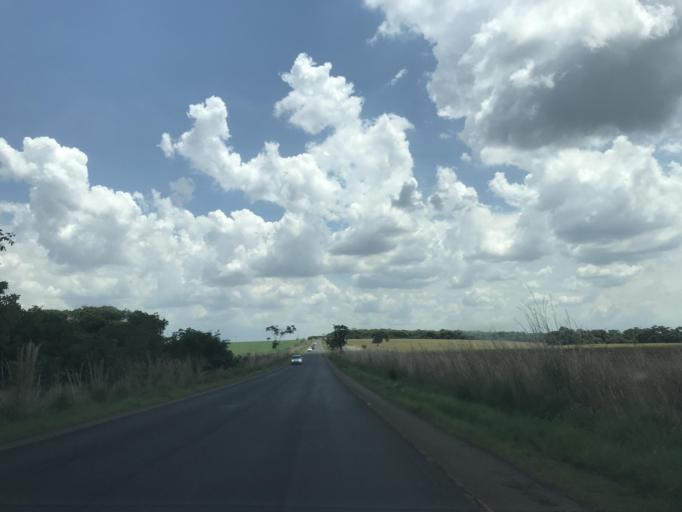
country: BR
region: Goias
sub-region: Piracanjuba
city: Piracanjuba
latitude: -17.3524
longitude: -48.7944
